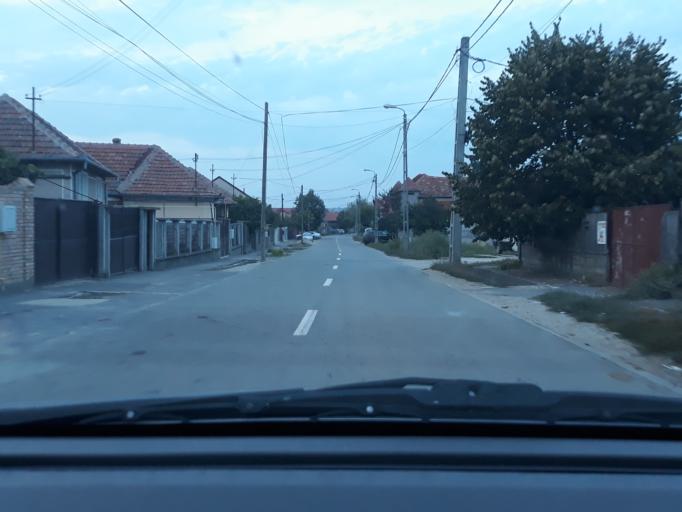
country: RO
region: Bihor
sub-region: Comuna Biharea
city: Oradea
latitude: 47.0279
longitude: 21.9358
